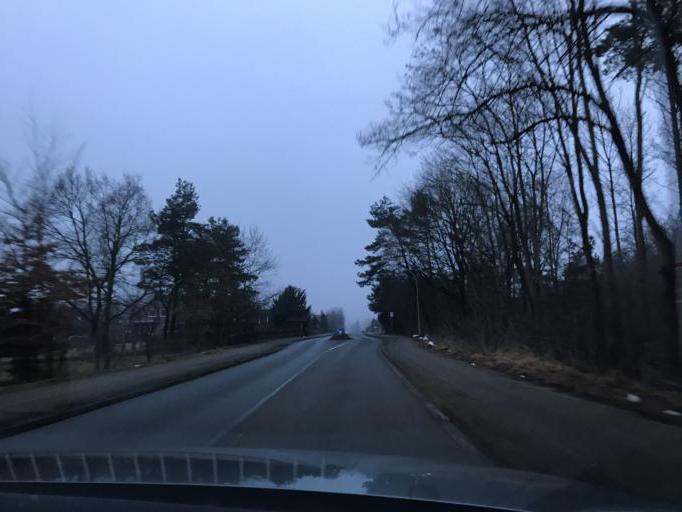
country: DE
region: Lower Saxony
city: Munster
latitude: 52.9983
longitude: 10.1030
